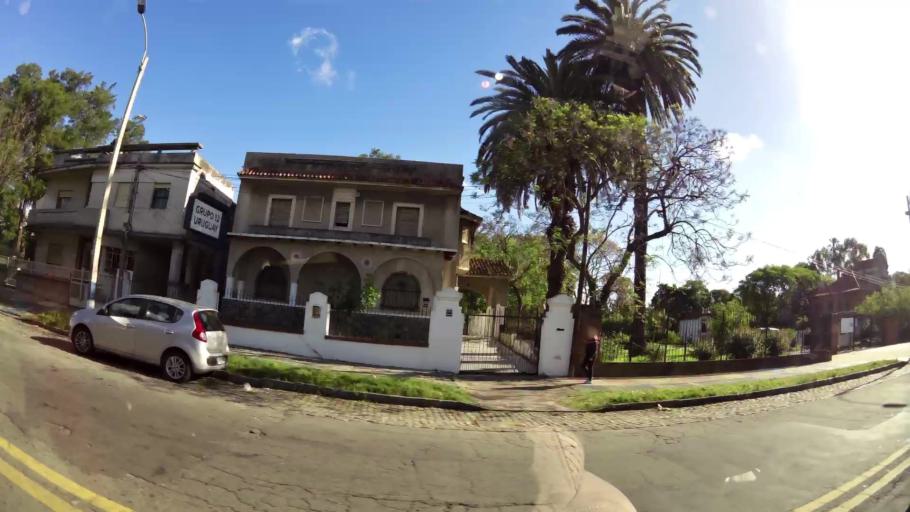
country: UY
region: Montevideo
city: Montevideo
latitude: -34.8574
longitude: -56.1992
